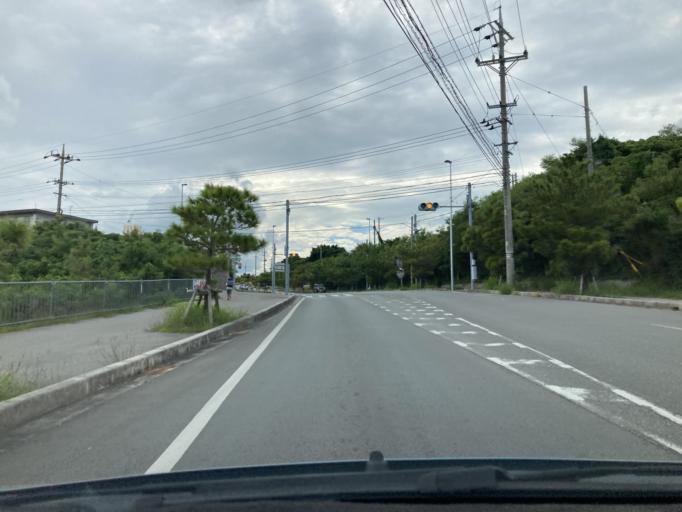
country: JP
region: Okinawa
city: Katsuren-haebaru
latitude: 26.3283
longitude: 127.8950
